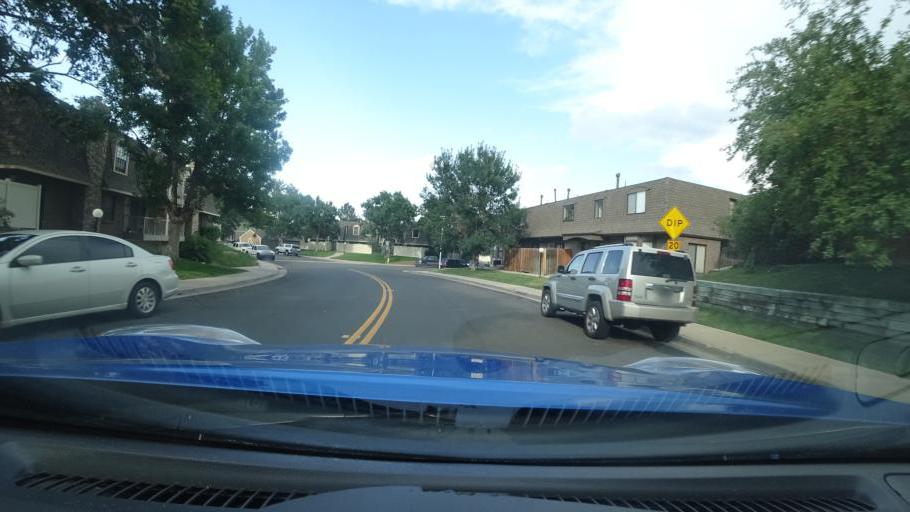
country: US
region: Colorado
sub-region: Adams County
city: Aurora
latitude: 39.6918
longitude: -104.8072
